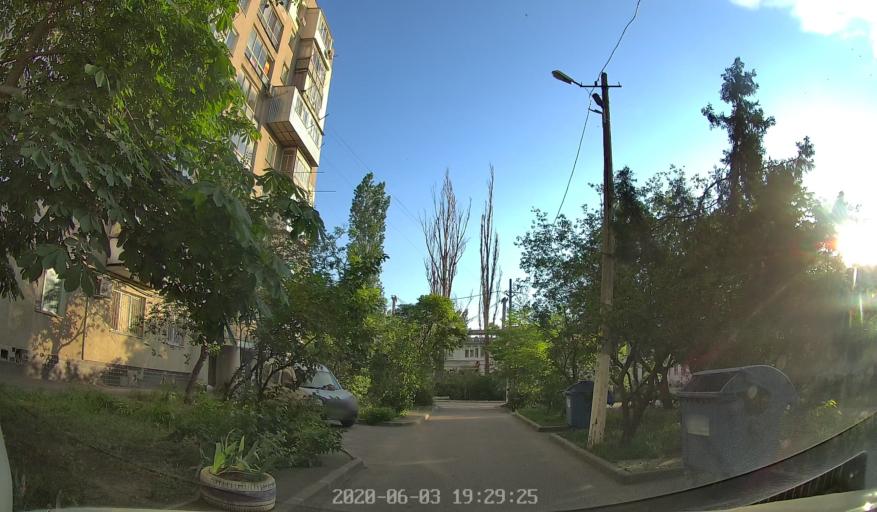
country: BG
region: Burgas
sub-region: Obshtina Malko Turnovo
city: Malko Turnovo
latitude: 41.9007
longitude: 27.6870
